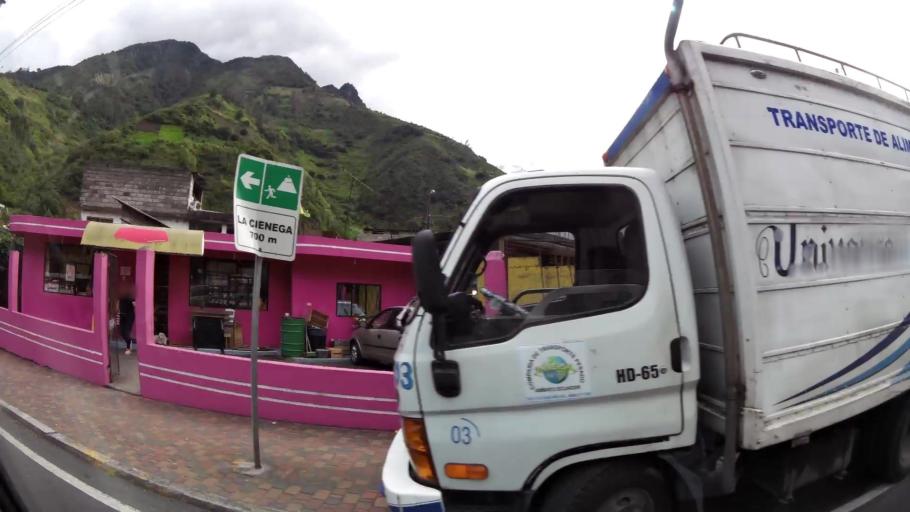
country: EC
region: Tungurahua
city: Banos
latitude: -1.3950
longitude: -78.3938
